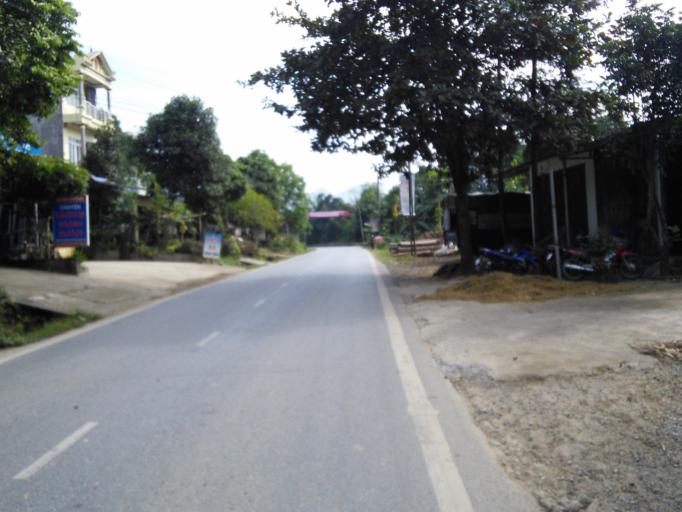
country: VN
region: Lao Cai
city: Lao Cai
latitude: 22.4629
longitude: 103.9475
